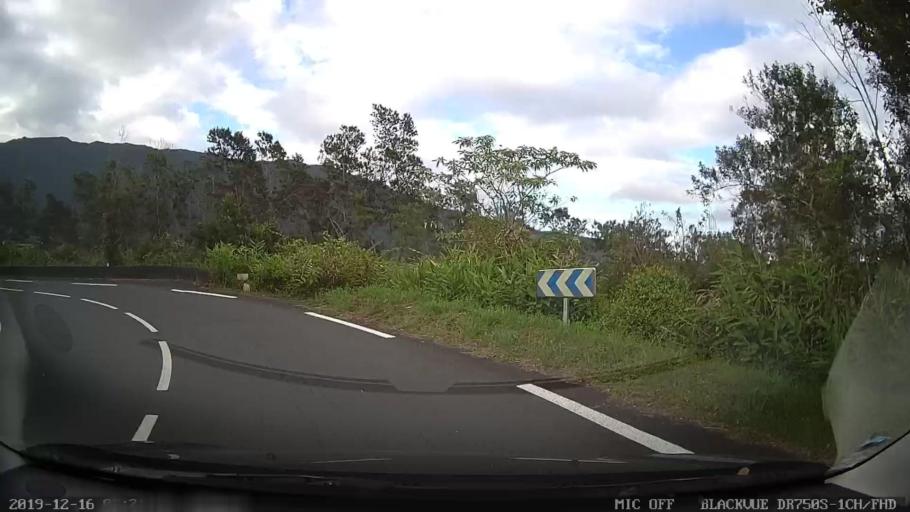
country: RE
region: Reunion
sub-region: Reunion
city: Cilaos
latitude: -21.1500
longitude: 55.6154
